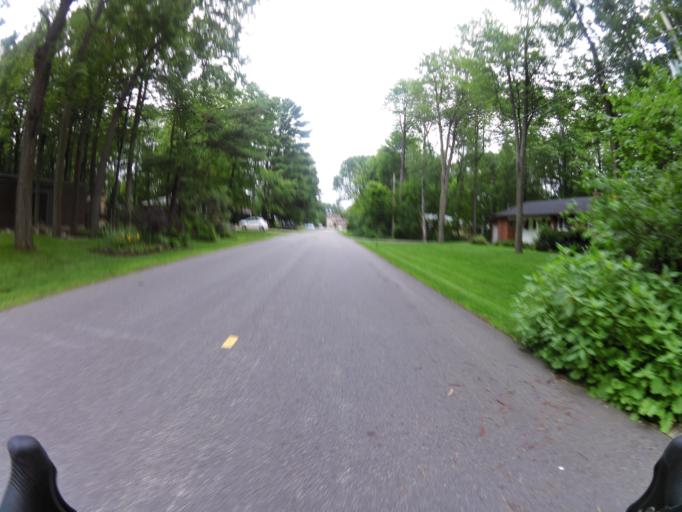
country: CA
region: Ontario
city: Ottawa
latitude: 45.3258
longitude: -75.7069
